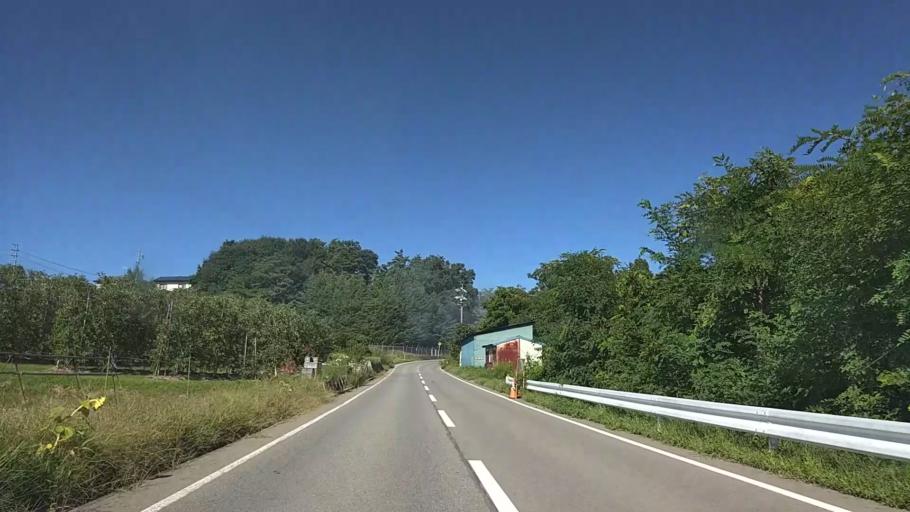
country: JP
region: Nagano
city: Nagano-shi
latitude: 36.5798
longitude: 138.1118
